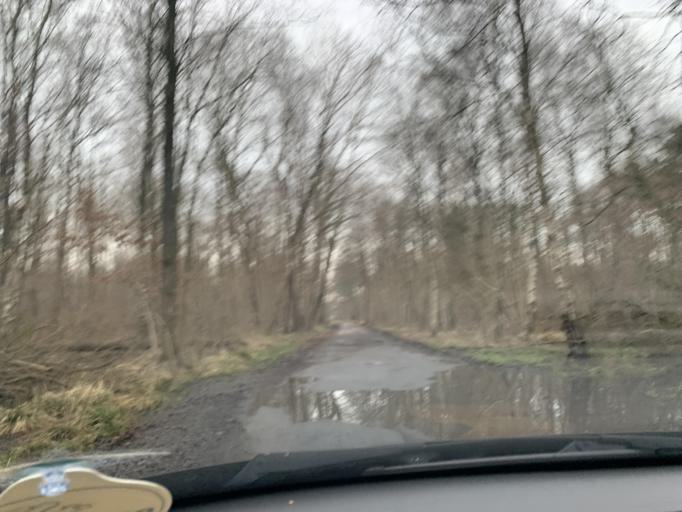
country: DE
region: Lower Saxony
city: Bad Zwischenahn
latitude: 53.2112
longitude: 7.9883
